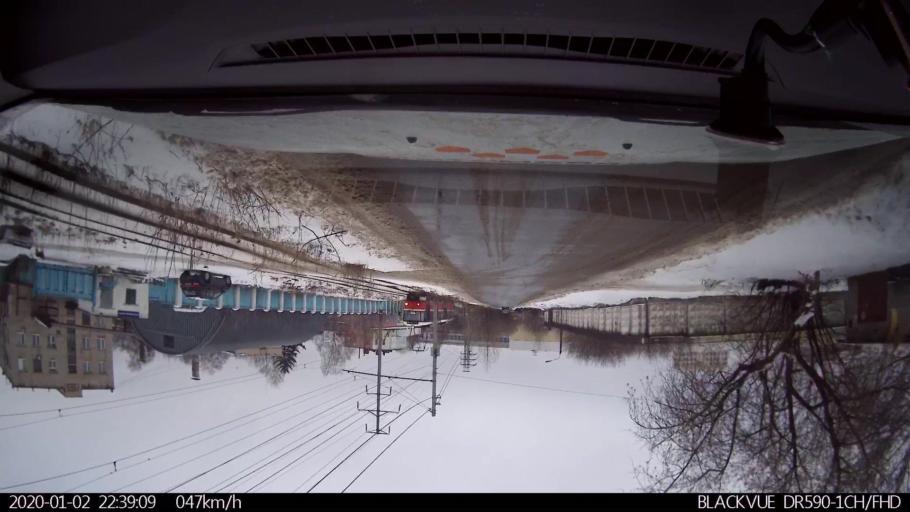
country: RU
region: Nizjnij Novgorod
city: Nizhniy Novgorod
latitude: 56.3333
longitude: 43.9064
